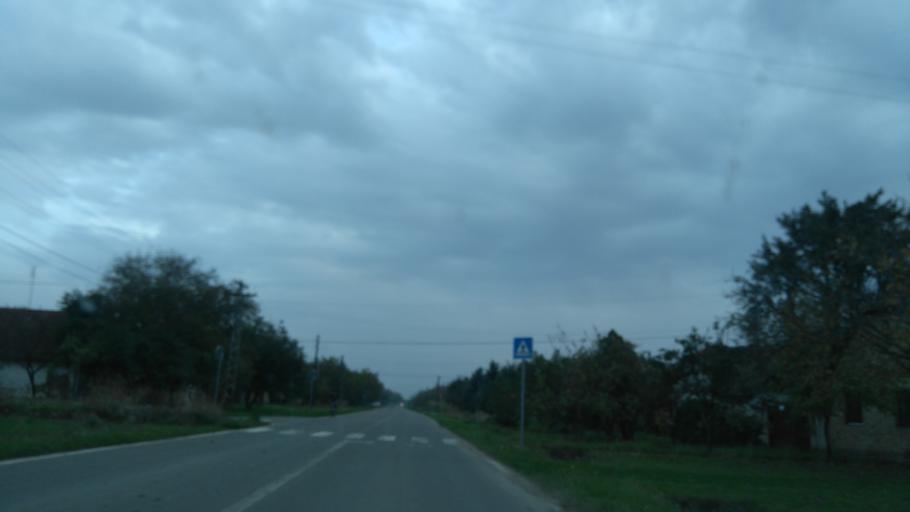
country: RS
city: Mol
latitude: 45.7706
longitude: 20.1233
